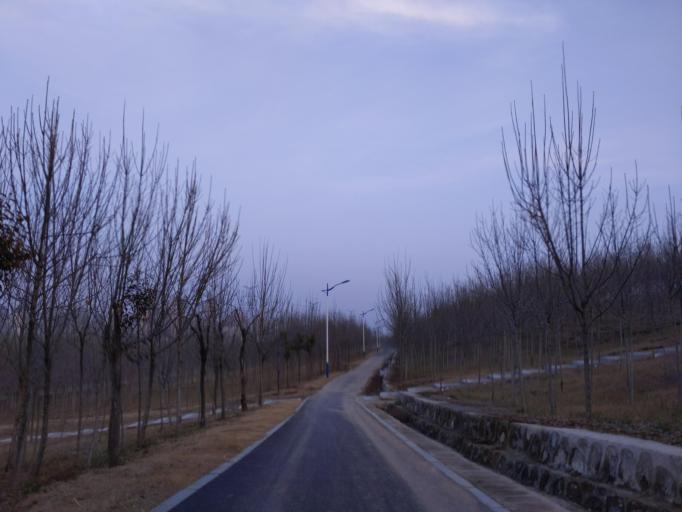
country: CN
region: Henan Sheng
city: Zhongyuanlu
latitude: 35.8187
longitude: 115.0487
